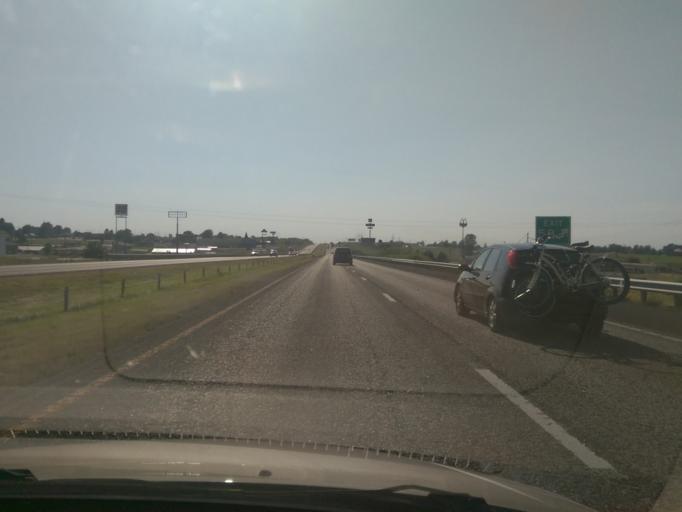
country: US
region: Missouri
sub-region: Lafayette County
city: Concordia
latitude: 38.9917
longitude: -93.5647
